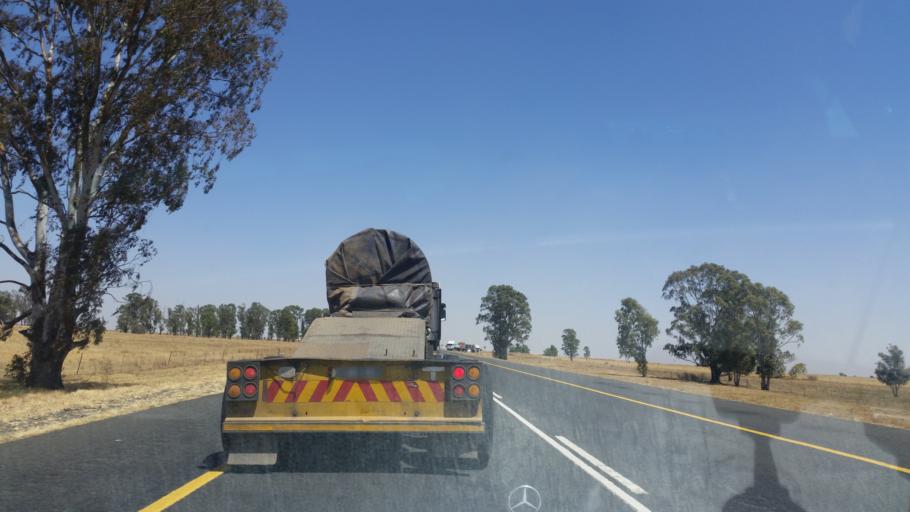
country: ZA
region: Orange Free State
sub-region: Lejweleputswa District Municipality
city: Winburg
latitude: -28.6402
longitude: 26.8909
